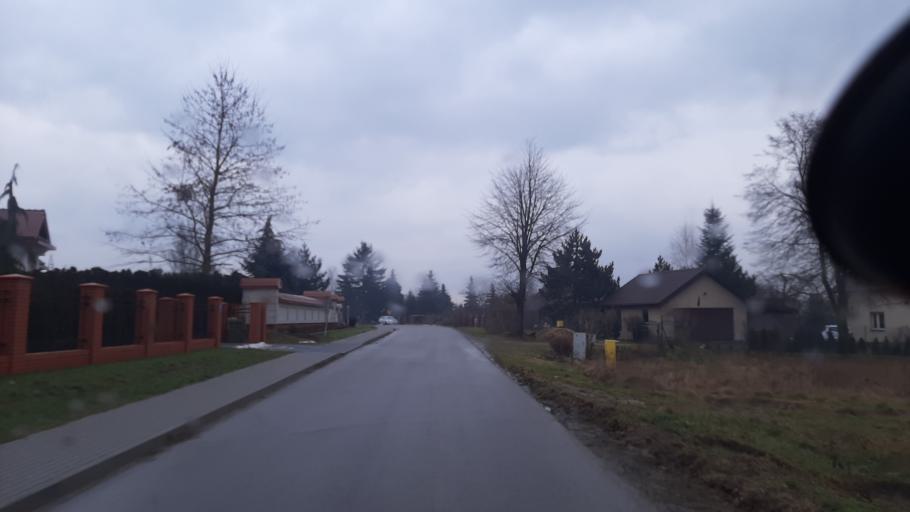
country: PL
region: Lublin Voivodeship
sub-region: Powiat lubelski
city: Niemce
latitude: 51.3187
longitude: 22.5883
